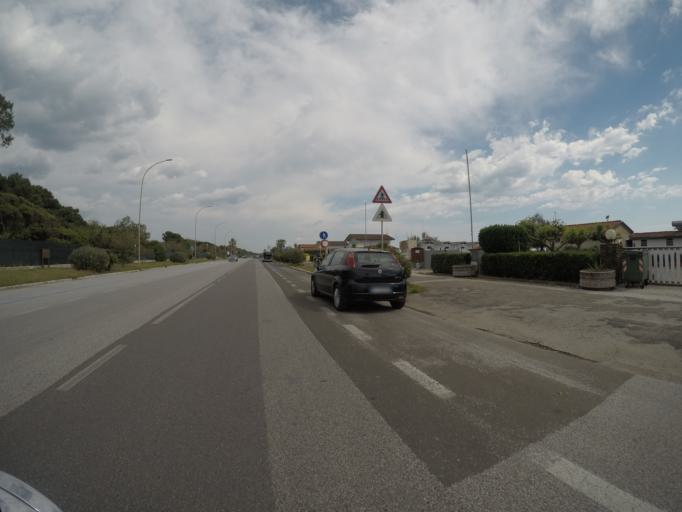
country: IT
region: Tuscany
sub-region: Provincia di Massa-Carrara
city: Massa
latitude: 43.9976
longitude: 10.1156
